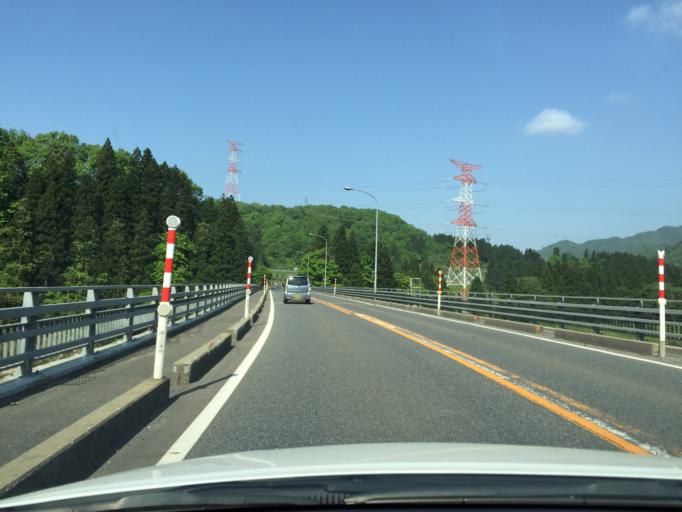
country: JP
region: Niigata
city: Suibara
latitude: 37.7350
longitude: 139.3270
